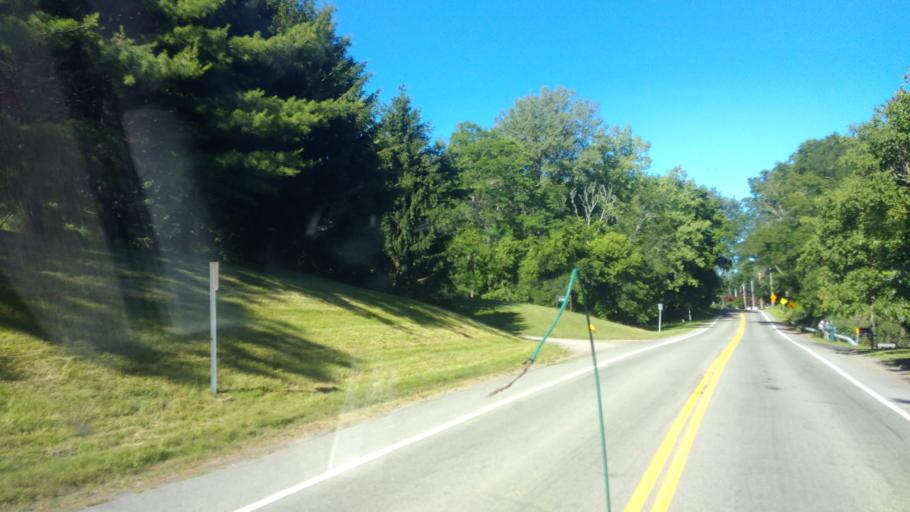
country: US
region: New York
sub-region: Monroe County
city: Webster
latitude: 43.2594
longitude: -77.4526
